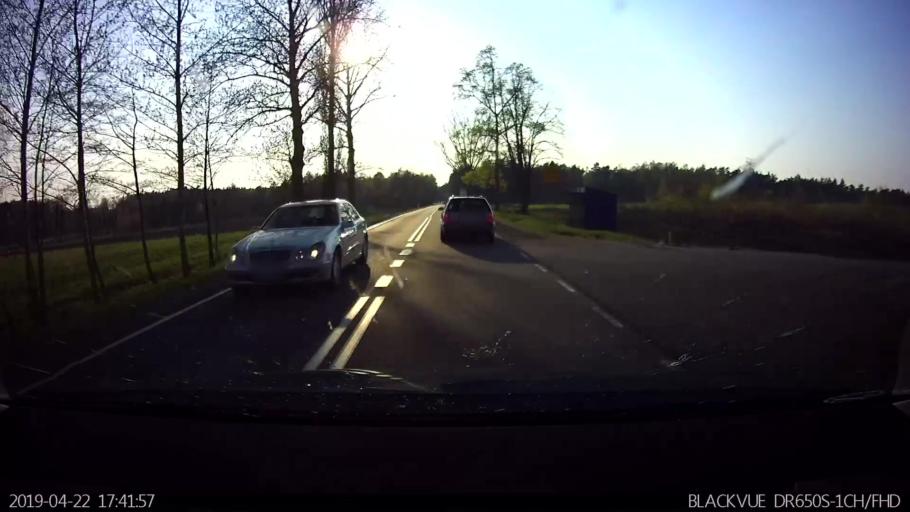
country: PL
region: Masovian Voivodeship
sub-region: Powiat wegrowski
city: Miedzna
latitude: 52.4036
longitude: 22.0925
